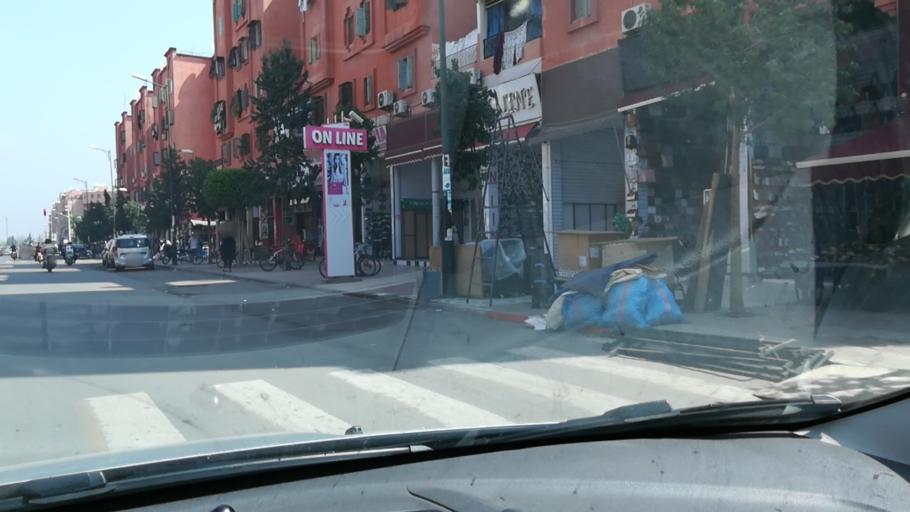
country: MA
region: Marrakech-Tensift-Al Haouz
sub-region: Marrakech
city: Marrakesh
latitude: 31.6322
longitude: -8.0583
